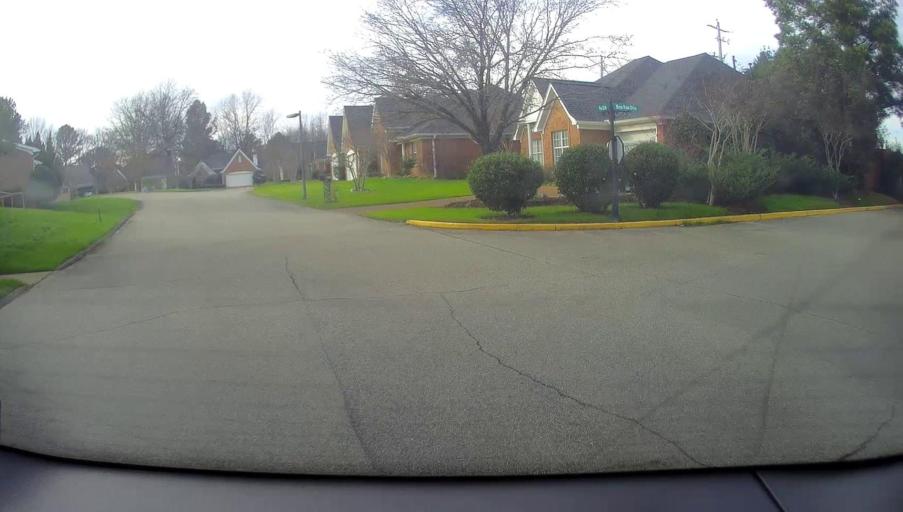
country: US
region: Tennessee
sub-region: Shelby County
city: Germantown
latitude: 35.0575
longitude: -89.8517
